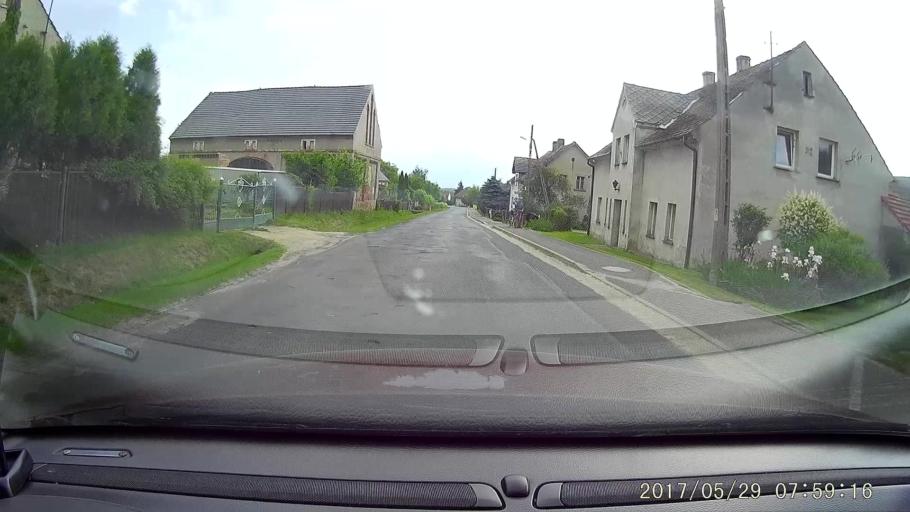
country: PL
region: Lower Silesian Voivodeship
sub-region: Powiat zlotoryjski
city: Olszanica
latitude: 51.2042
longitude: 15.7949
